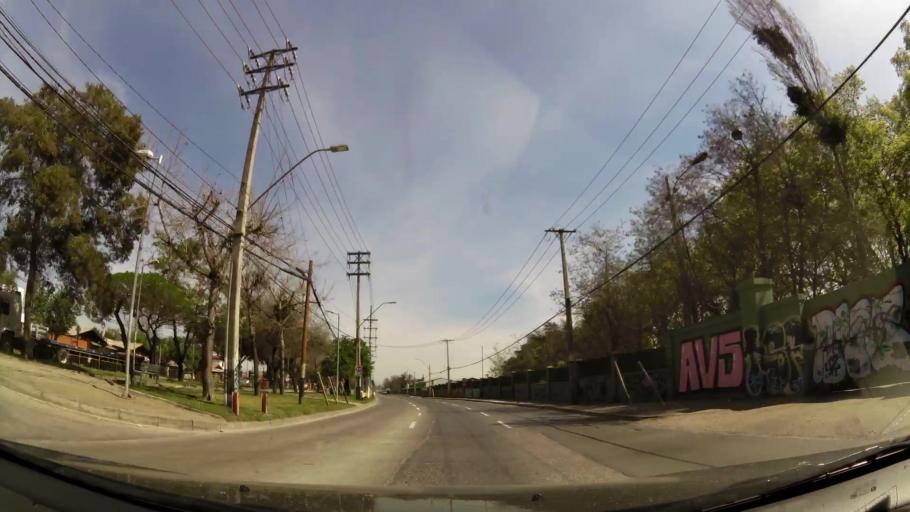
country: CL
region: Santiago Metropolitan
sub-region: Provincia de Cordillera
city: Puente Alto
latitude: -33.6100
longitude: -70.5583
